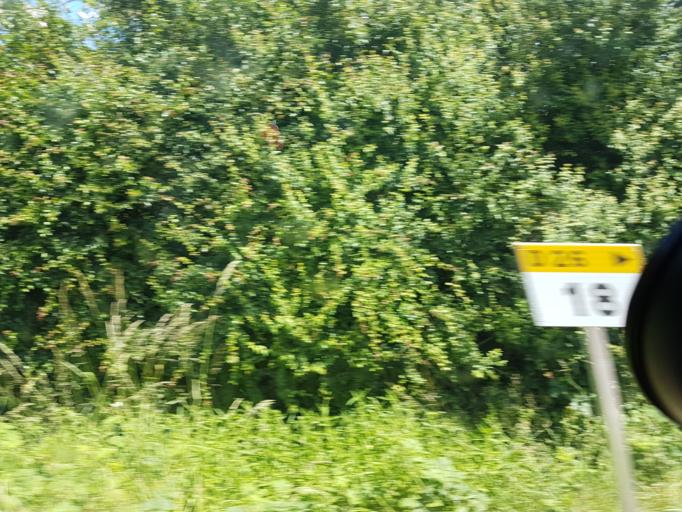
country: FR
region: Bourgogne
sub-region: Departement de Saone-et-Loire
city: Epinac
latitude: 47.0062
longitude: 4.4622
